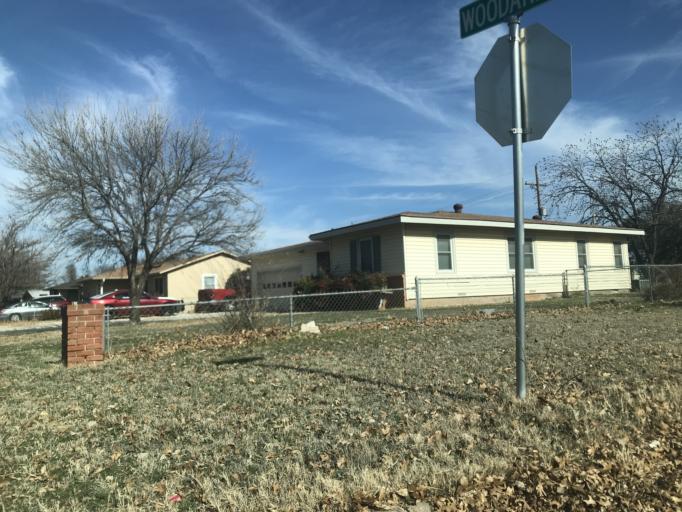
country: US
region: Texas
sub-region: Taylor County
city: Abilene
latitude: 32.4231
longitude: -99.7584
